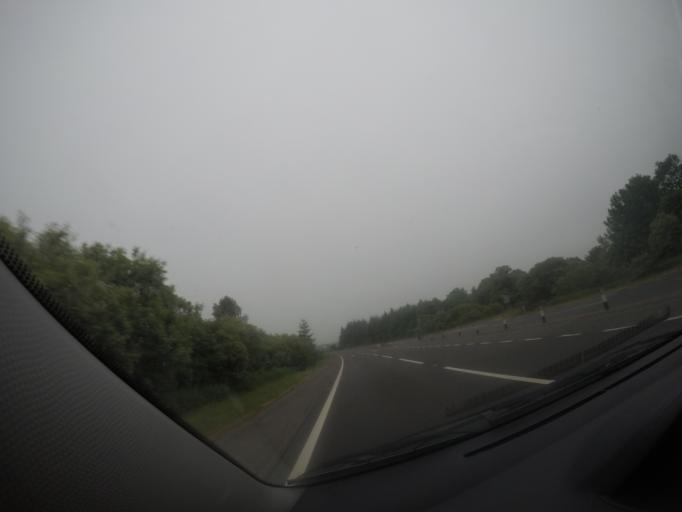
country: GB
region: Scotland
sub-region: Angus
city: Forfar
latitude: 56.5560
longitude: -2.9276
